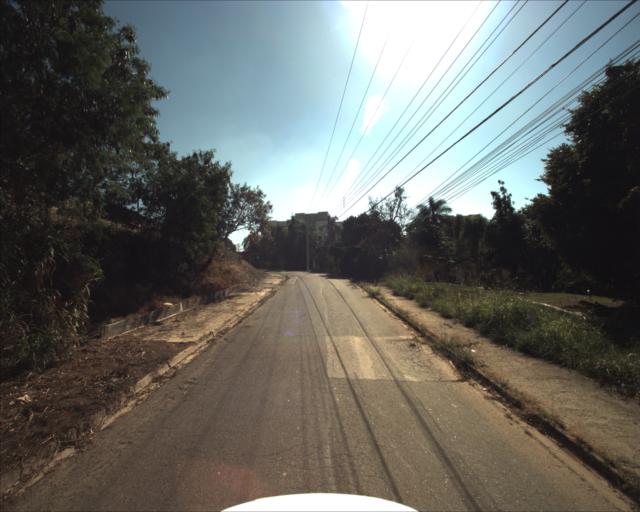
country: BR
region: Sao Paulo
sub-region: Sorocaba
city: Sorocaba
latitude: -23.4947
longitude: -47.4174
